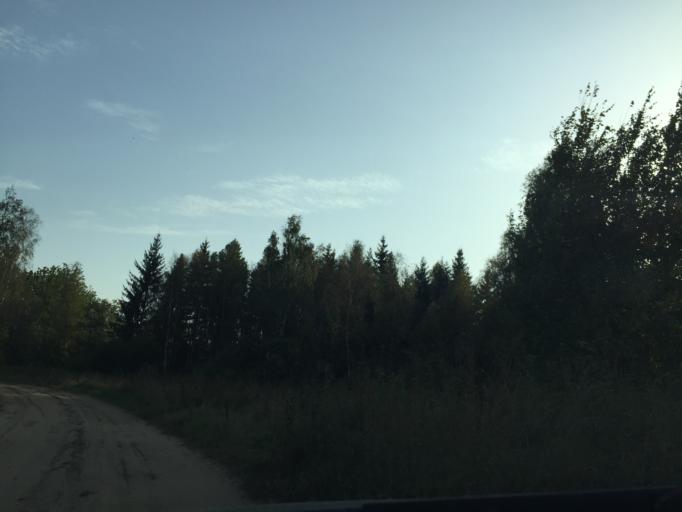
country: LV
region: Garkalne
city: Garkalne
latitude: 56.9716
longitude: 24.4171
